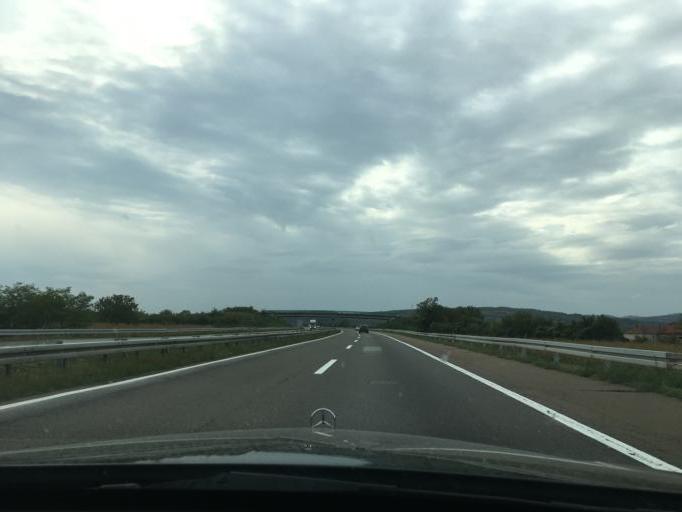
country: RS
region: Central Serbia
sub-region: Sumadijski Okrug
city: Batocina
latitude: 44.1271
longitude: 21.1380
